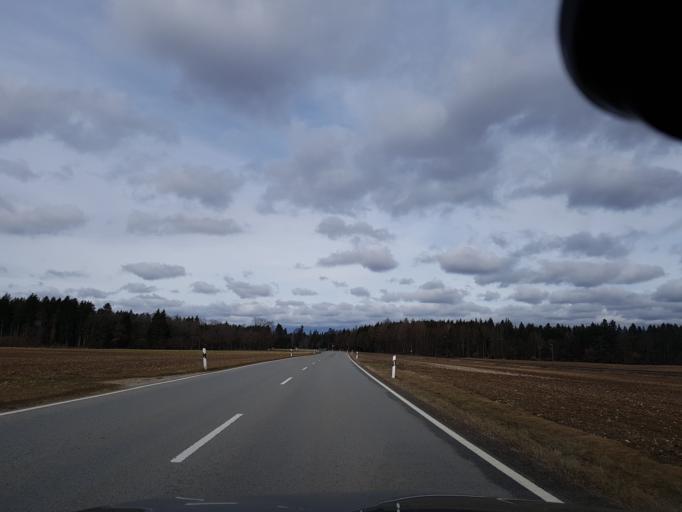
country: DE
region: Bavaria
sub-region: Upper Bavaria
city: Aying
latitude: 47.9765
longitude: 11.7579
